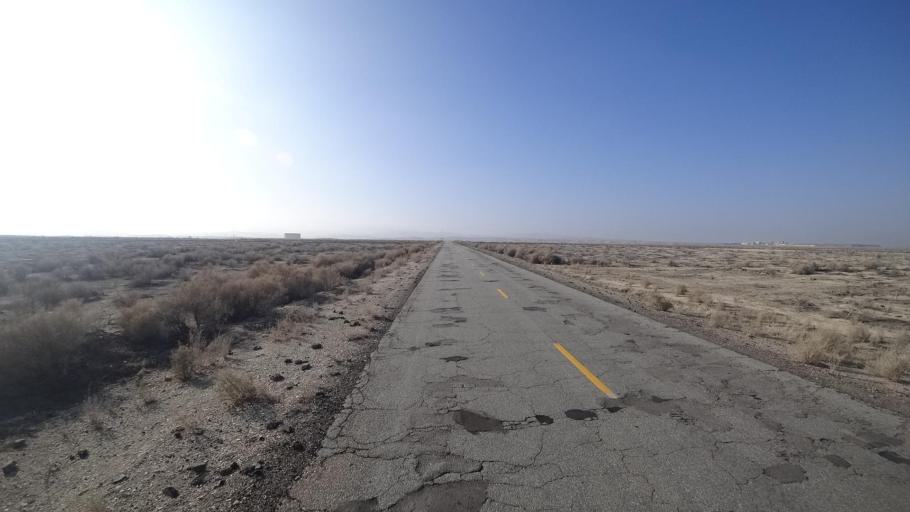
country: US
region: California
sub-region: Kern County
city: Maricopa
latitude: 35.1011
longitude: -119.3845
